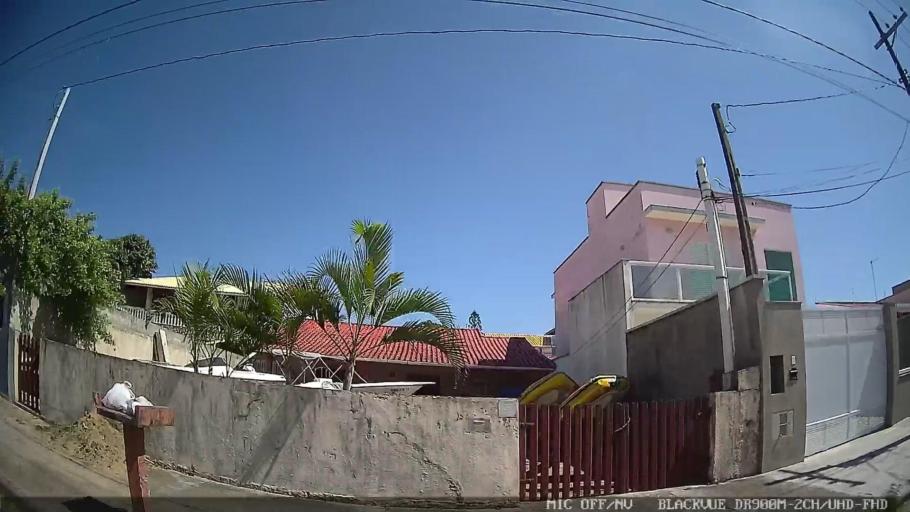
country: BR
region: Sao Paulo
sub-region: Peruibe
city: Peruibe
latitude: -24.3037
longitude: -46.9726
